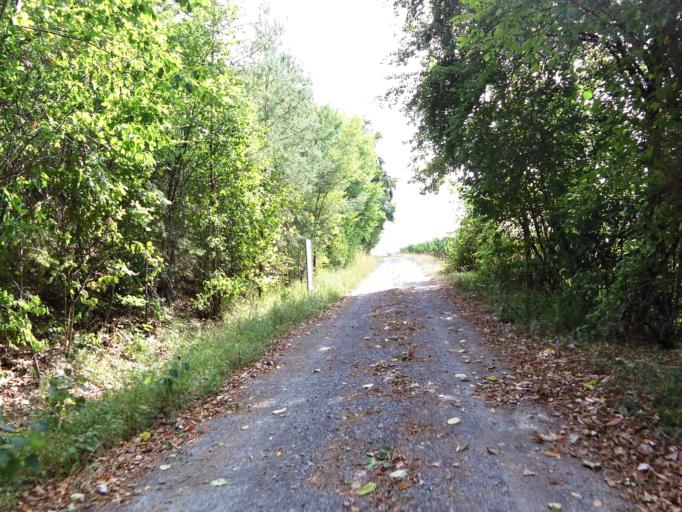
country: DE
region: Bavaria
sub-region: Regierungsbezirk Unterfranken
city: Margetshochheim
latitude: 49.8487
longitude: 9.8697
